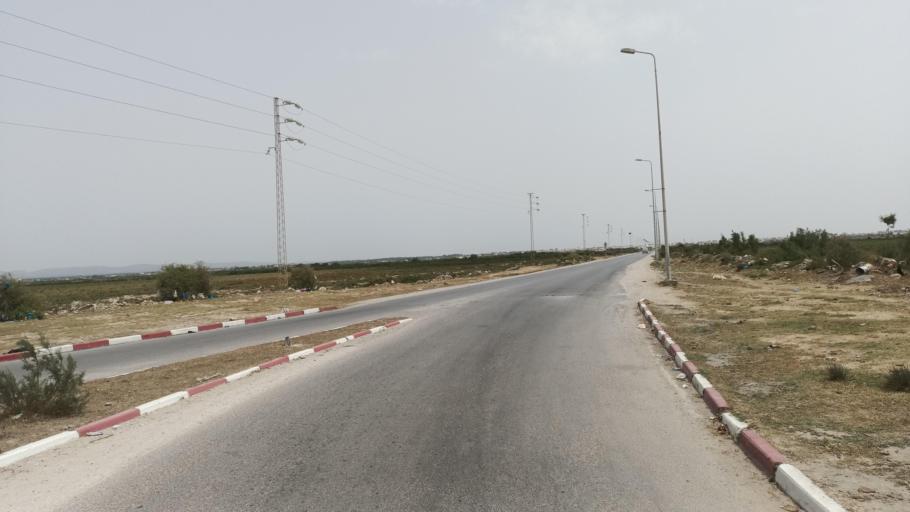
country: TN
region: Nabul
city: Manzil Bu Zalafah
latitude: 36.7260
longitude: 10.4701
